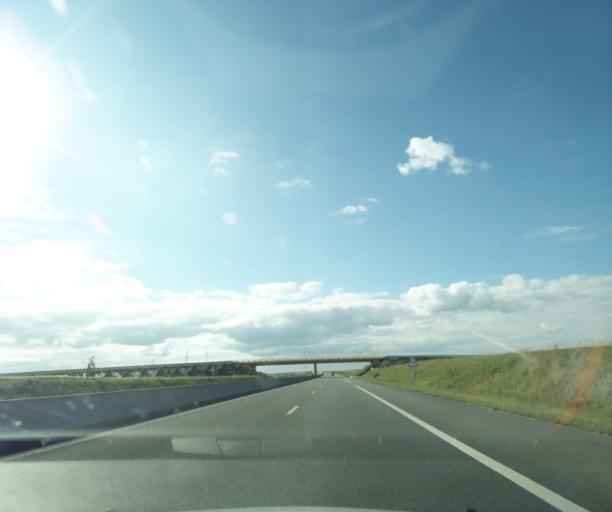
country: FR
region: Centre
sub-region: Departement d'Eure-et-Loir
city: Sours
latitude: 48.3462
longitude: 1.6287
